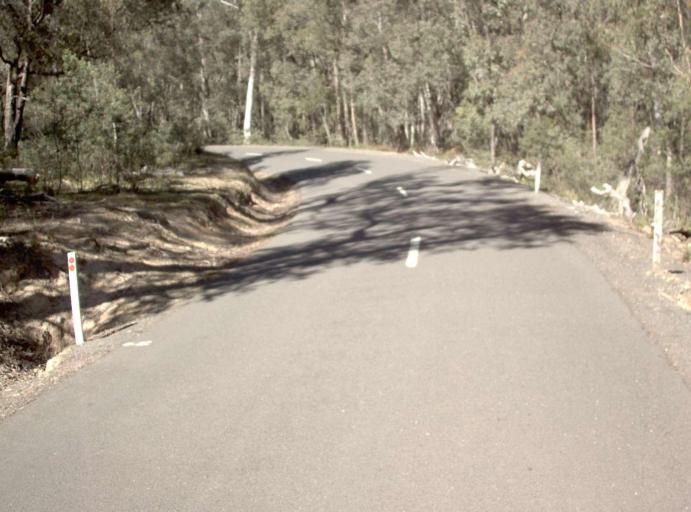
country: AU
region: New South Wales
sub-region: Bombala
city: Bombala
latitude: -37.1110
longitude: 148.7562
